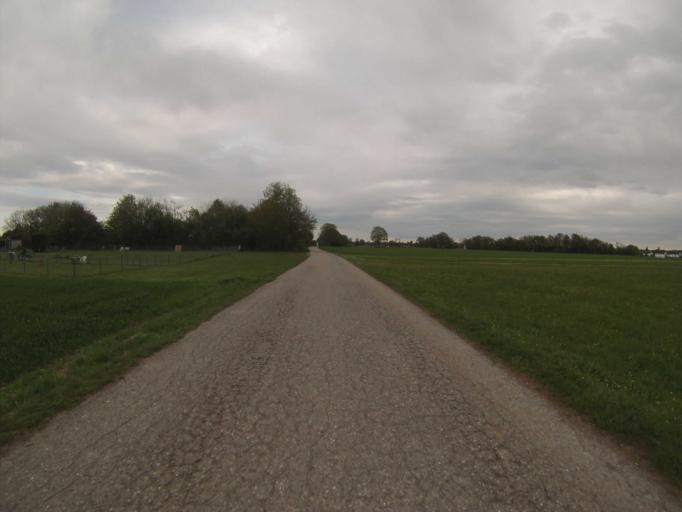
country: DE
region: Bavaria
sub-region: Upper Bavaria
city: Sauerlach
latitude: 47.9763
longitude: 11.6395
